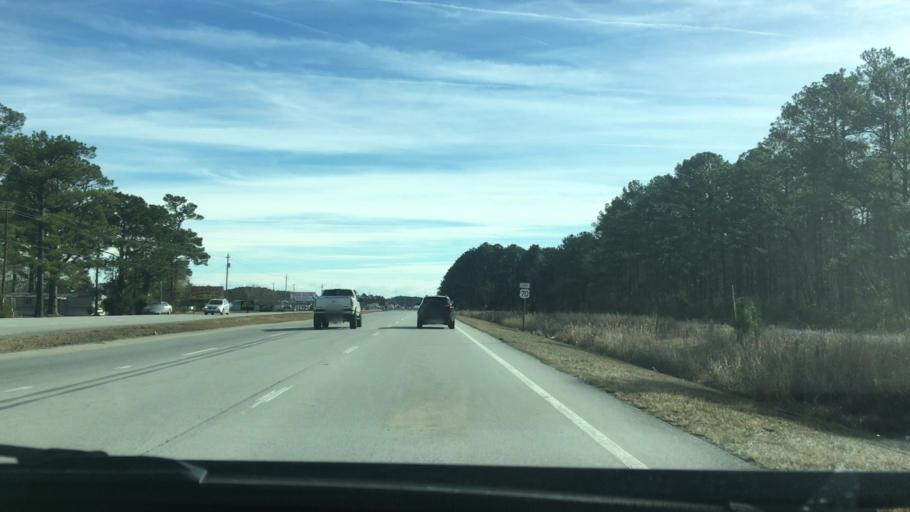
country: US
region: North Carolina
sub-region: Carteret County
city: Newport
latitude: 34.7603
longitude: -76.8526
